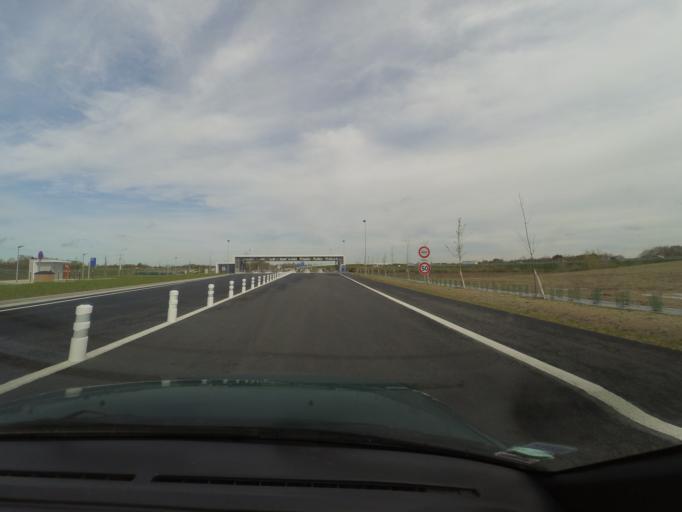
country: FR
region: Pays de la Loire
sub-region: Departement de la Loire-Atlantique
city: Aigrefeuille-sur-Maine
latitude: 47.0681
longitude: -1.4366
